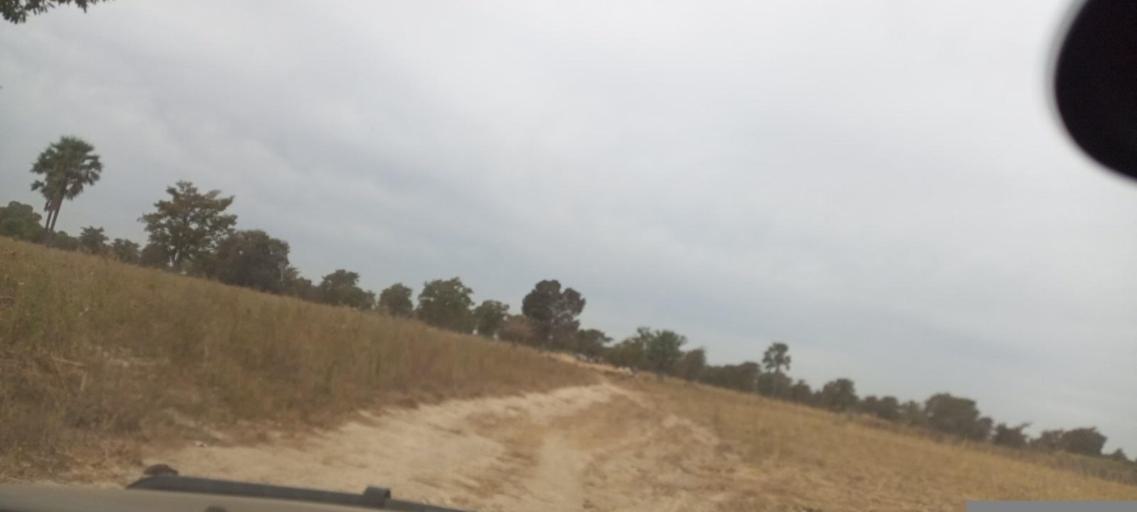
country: ML
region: Koulikoro
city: Kati
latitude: 12.7450
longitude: -8.3337
